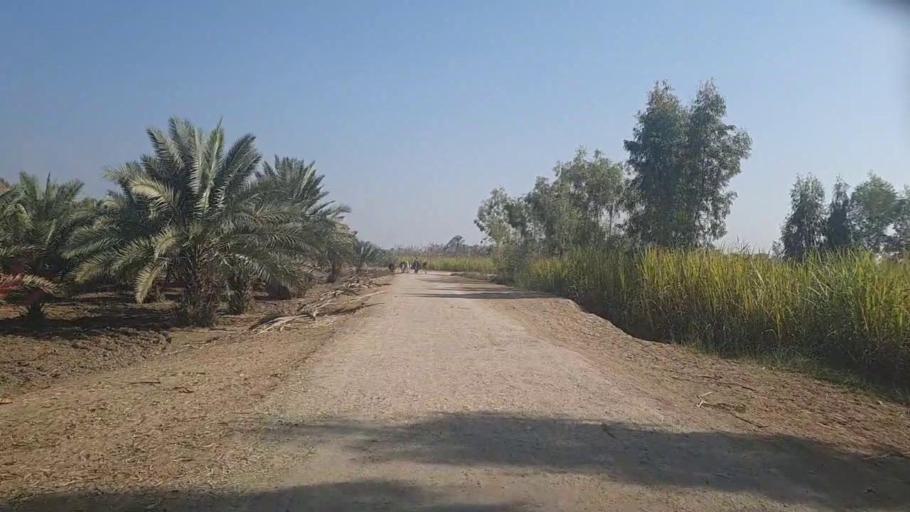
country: PK
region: Sindh
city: Kot Diji
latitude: 27.4297
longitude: 68.7365
